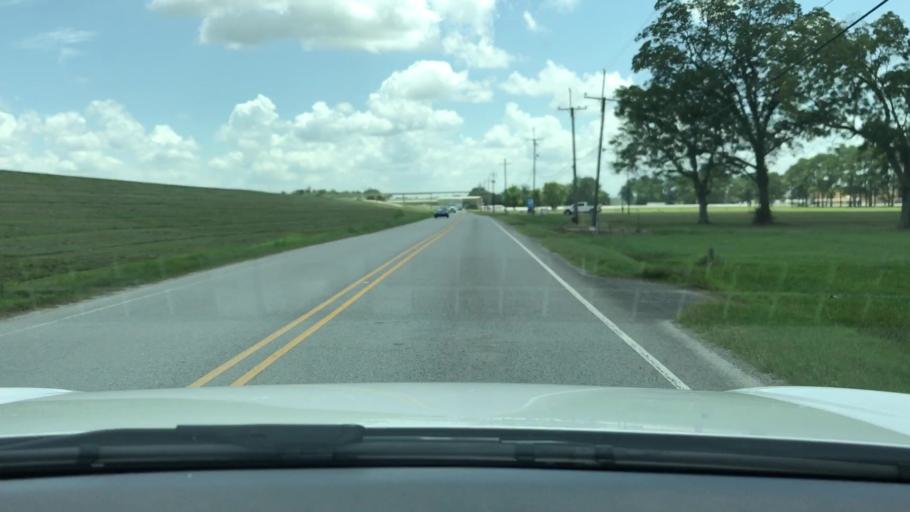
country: US
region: Louisiana
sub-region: Iberville Parish
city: Plaquemine
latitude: 30.2729
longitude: -91.1868
